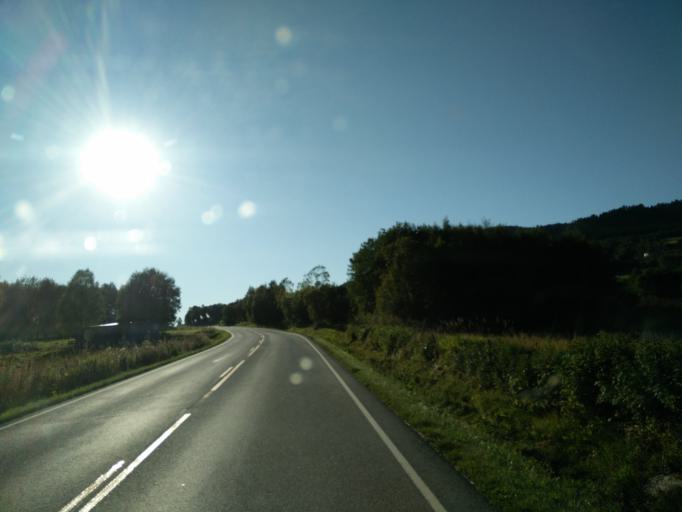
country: NO
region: More og Romsdal
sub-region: Halsa
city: Liaboen
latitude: 63.0725
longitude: 8.2690
